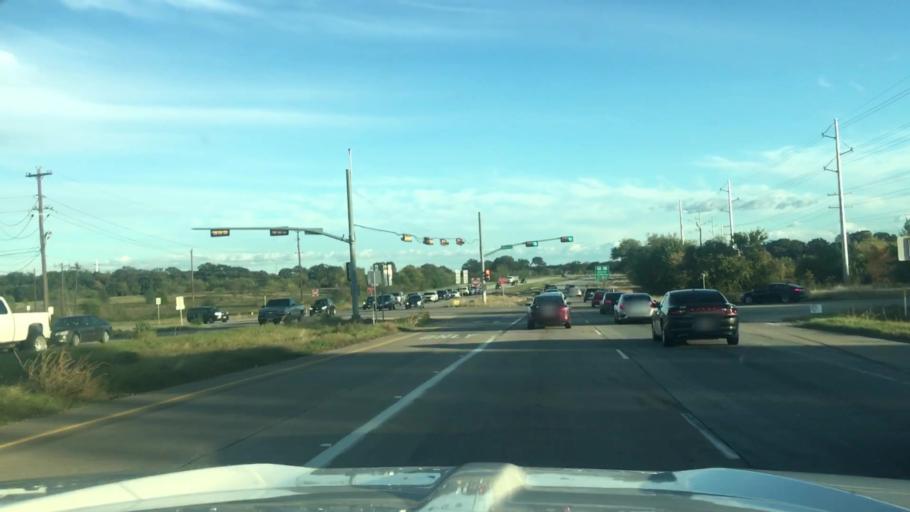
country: US
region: Texas
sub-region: Denton County
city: Denton
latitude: 33.2487
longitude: -97.0955
